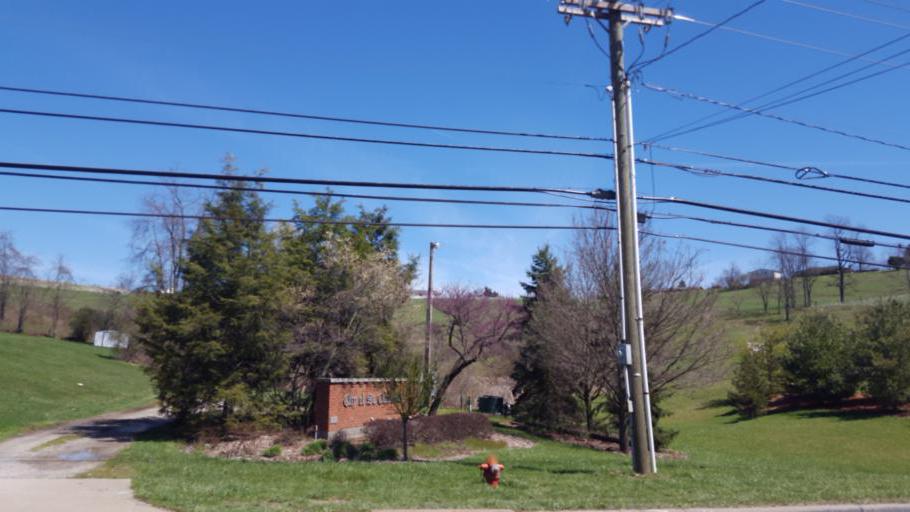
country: US
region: Ohio
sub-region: Belmont County
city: Saint Clairsville
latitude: 40.0798
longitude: -80.8770
